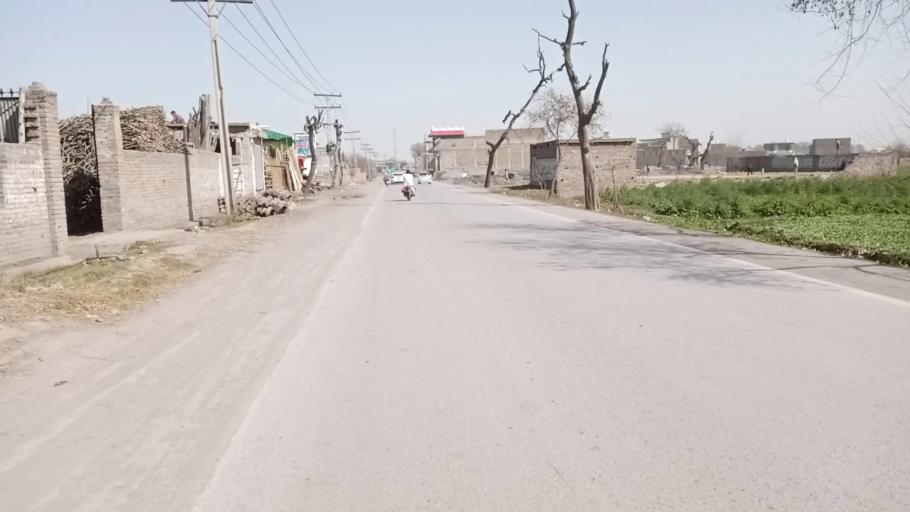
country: PK
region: Khyber Pakhtunkhwa
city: Peshawar
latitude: 33.9990
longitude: 71.6354
